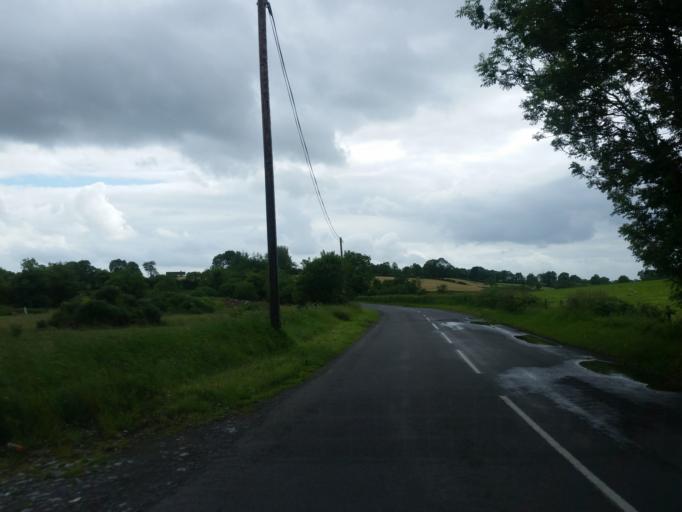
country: GB
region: Northern Ireland
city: Lisnaskea
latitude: 54.3008
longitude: -7.4168
